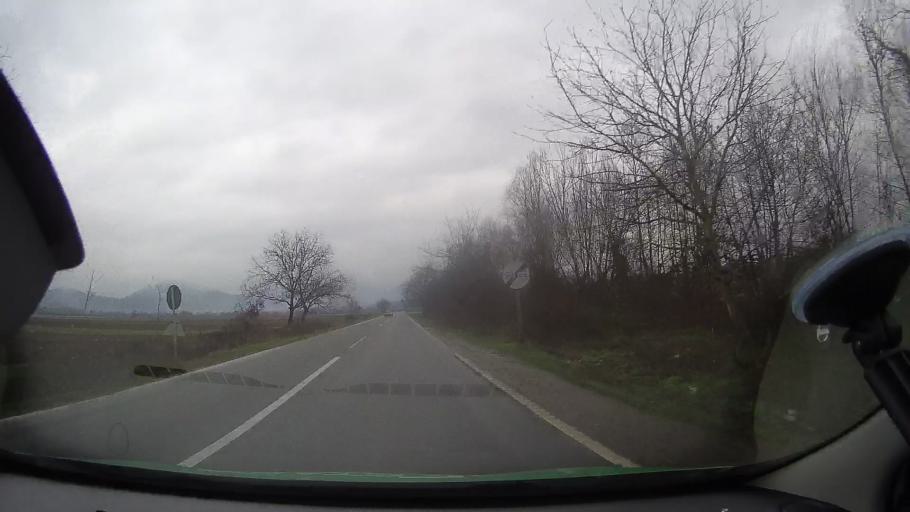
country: RO
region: Arad
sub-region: Comuna Gurahont
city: Gurahont
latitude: 46.2717
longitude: 22.3117
